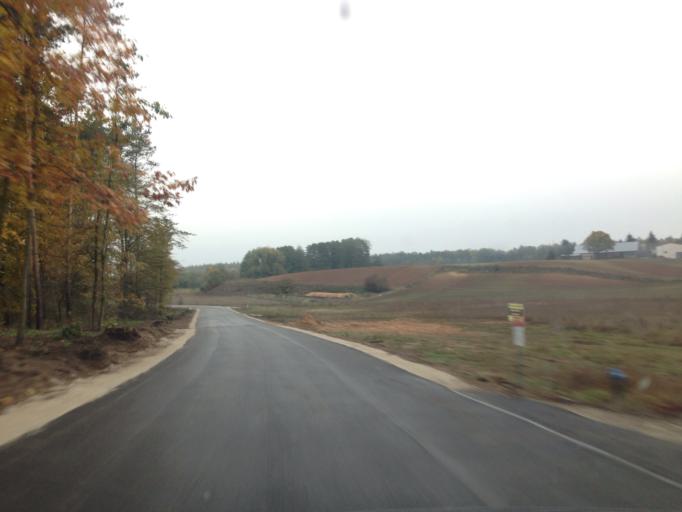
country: PL
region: Kujawsko-Pomorskie
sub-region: Powiat brodnicki
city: Bobrowo
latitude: 53.2600
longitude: 19.2996
